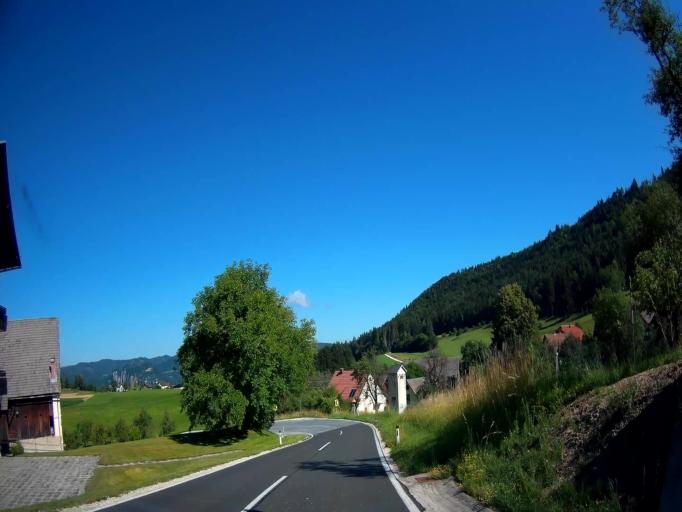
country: AT
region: Carinthia
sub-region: Politischer Bezirk Klagenfurt Land
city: Grafenstein
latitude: 46.5388
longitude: 14.4457
